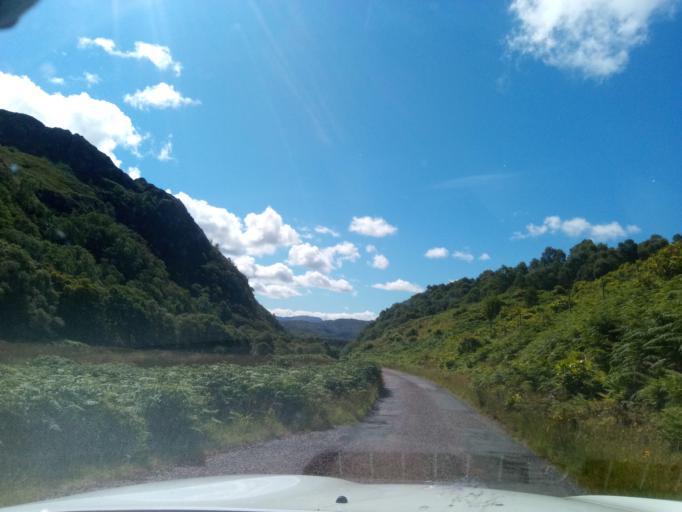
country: GB
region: Scotland
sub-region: Argyll and Bute
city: Isle Of Mull
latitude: 56.7730
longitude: -5.8246
